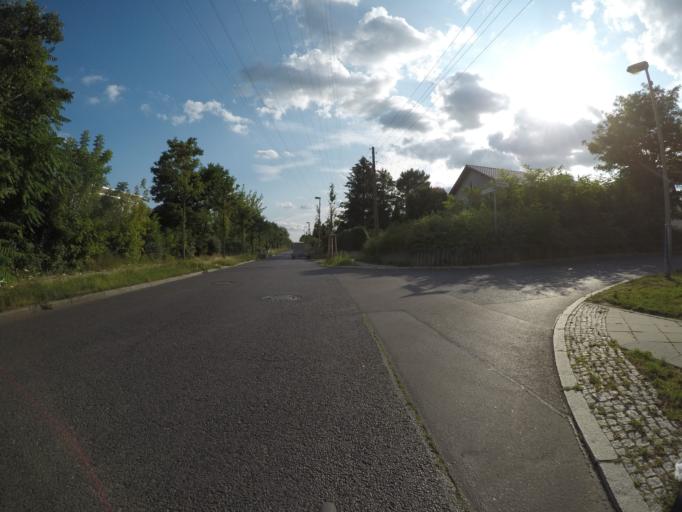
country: DE
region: Berlin
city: Kaulsdorf
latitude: 52.5211
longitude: 13.5989
